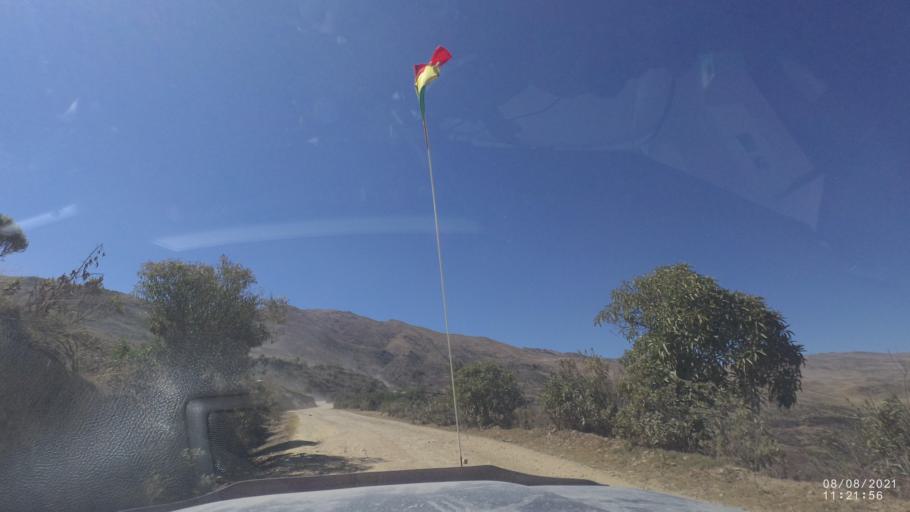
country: BO
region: Cochabamba
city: Colchani
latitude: -16.7779
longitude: -66.6519
